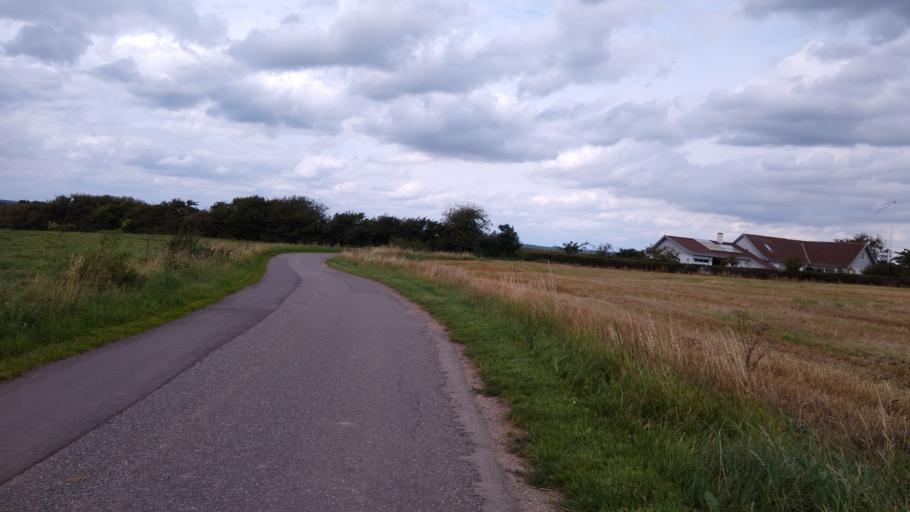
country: DK
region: South Denmark
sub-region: Fredericia Kommune
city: Fredericia
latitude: 55.6067
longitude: 9.7801
